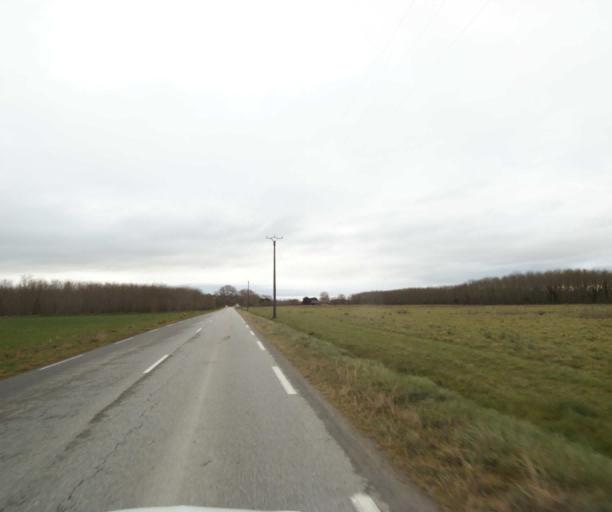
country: FR
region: Midi-Pyrenees
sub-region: Departement de l'Ariege
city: Saverdun
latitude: 43.2306
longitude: 1.6176
